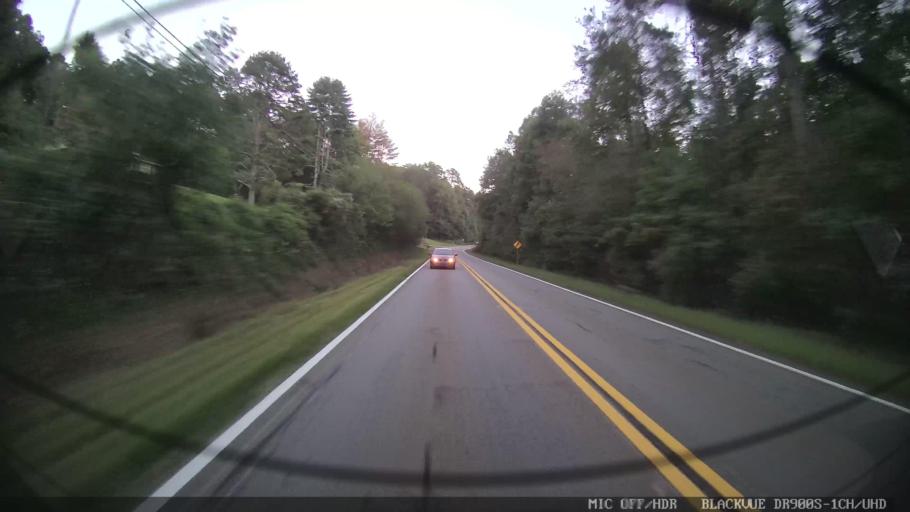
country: US
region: Georgia
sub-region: Gilmer County
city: Ellijay
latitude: 34.7210
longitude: -84.5039
